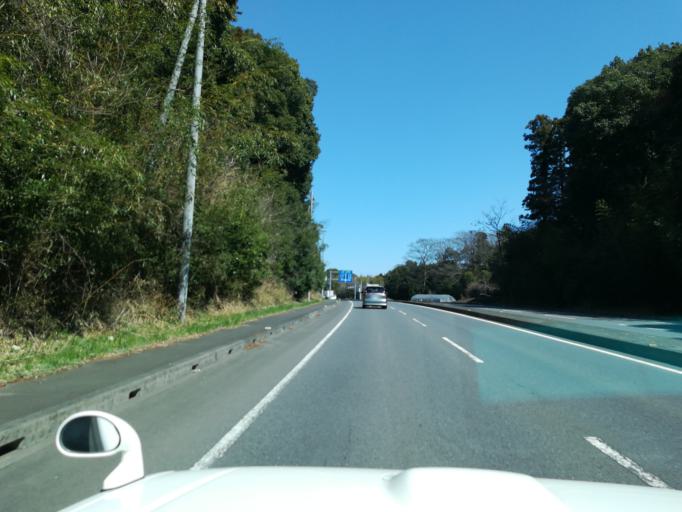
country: JP
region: Ibaraki
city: Ushiku
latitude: 35.9726
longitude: 140.1808
